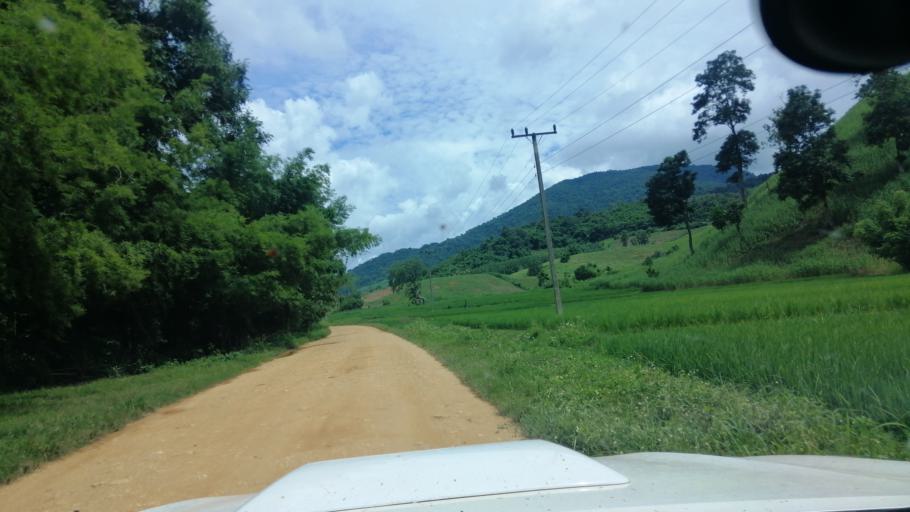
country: TH
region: Phayao
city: Phu Sang
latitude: 19.6803
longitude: 100.5031
